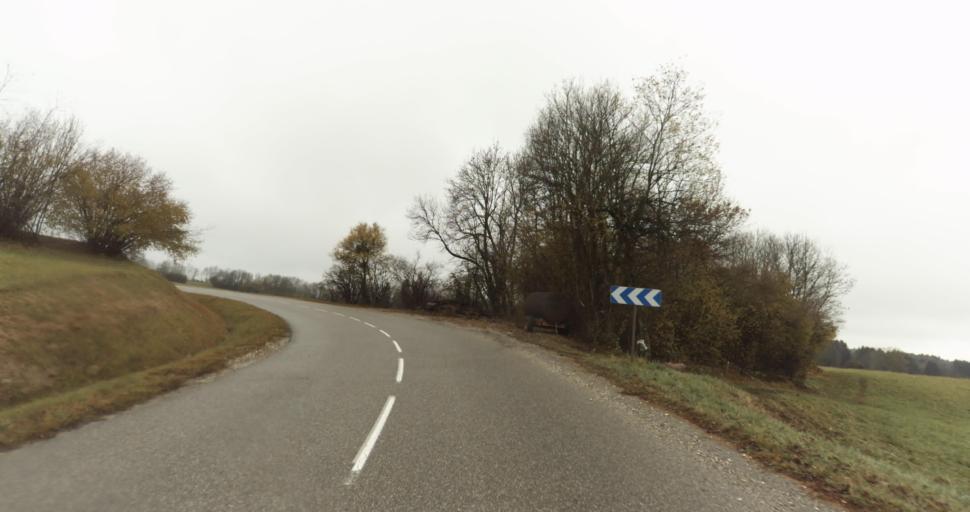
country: FR
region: Rhone-Alpes
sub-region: Departement de la Haute-Savoie
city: Etaux
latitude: 46.0288
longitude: 6.2828
